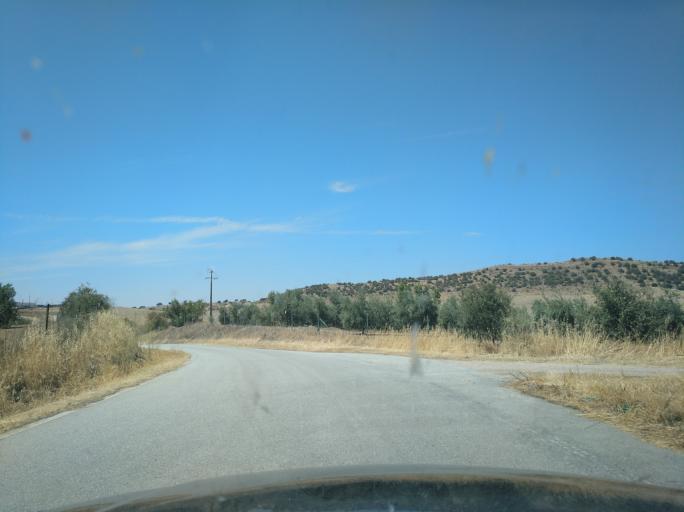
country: PT
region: Portalegre
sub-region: Campo Maior
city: Campo Maior
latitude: 38.9610
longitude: -7.1076
